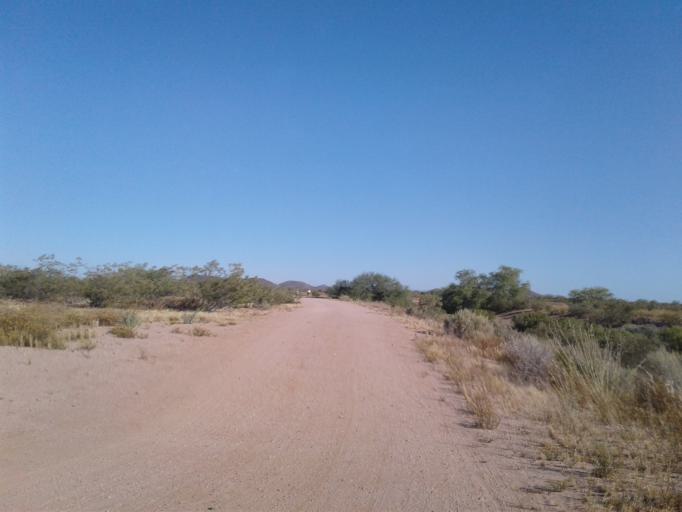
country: US
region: Arizona
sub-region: Maricopa County
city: Paradise Valley
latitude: 33.6756
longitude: -112.0103
